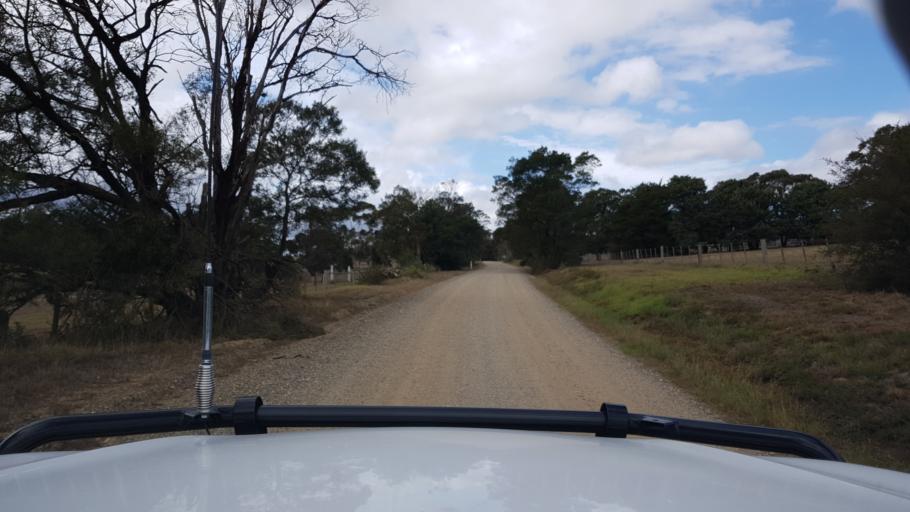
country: AU
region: Victoria
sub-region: East Gippsland
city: Bairnsdale
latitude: -37.7874
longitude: 147.5663
